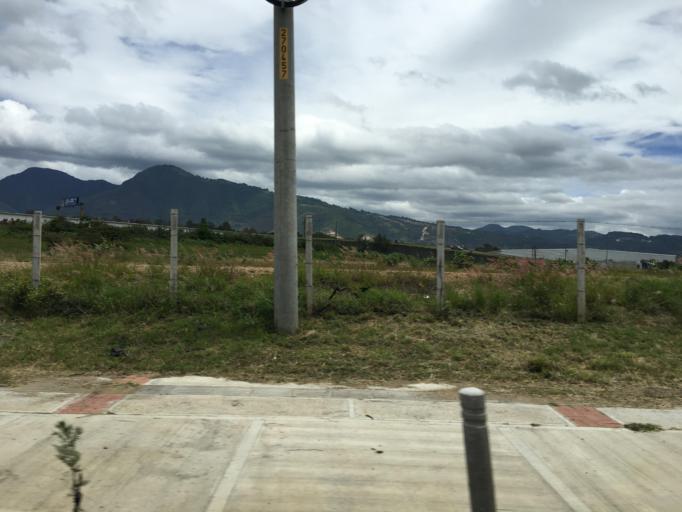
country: GT
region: Guatemala
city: Amatitlan
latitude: 14.5084
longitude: -90.6087
